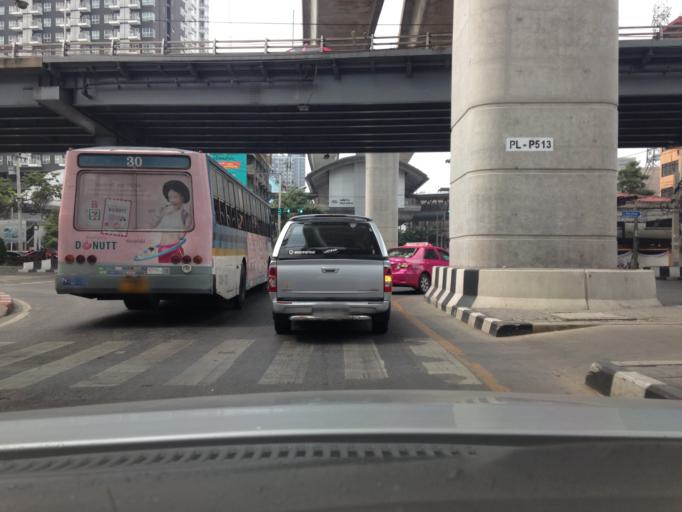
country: TH
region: Bangkok
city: Bang Sue
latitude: 13.8276
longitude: 100.5288
